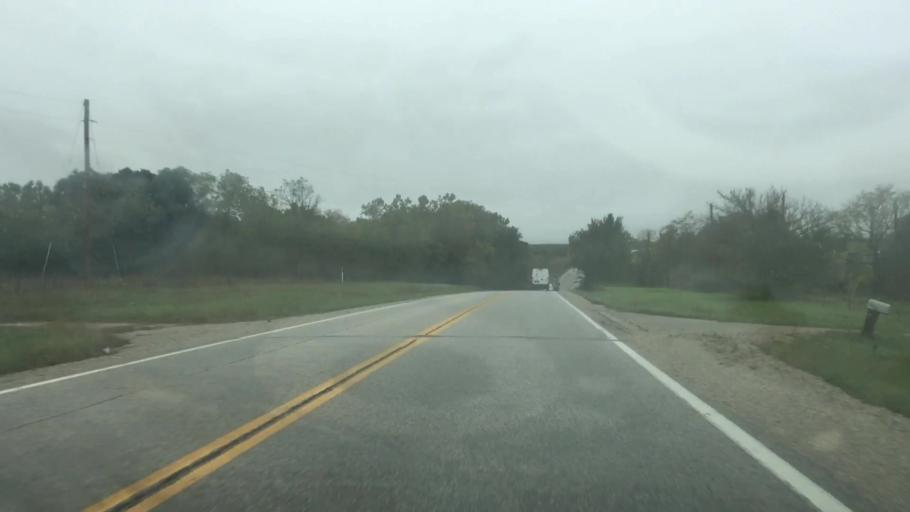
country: US
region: Kansas
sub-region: Anderson County
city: Garnett
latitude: 38.1930
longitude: -95.2527
